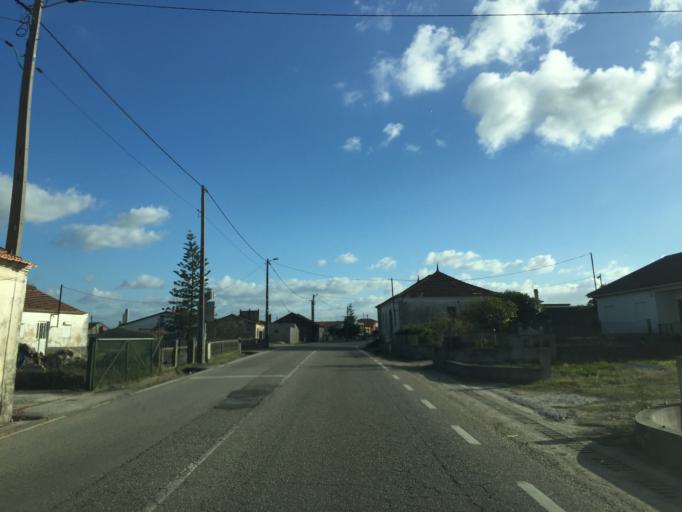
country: PT
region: Leiria
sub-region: Pombal
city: Lourical
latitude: 39.9829
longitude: -8.7990
